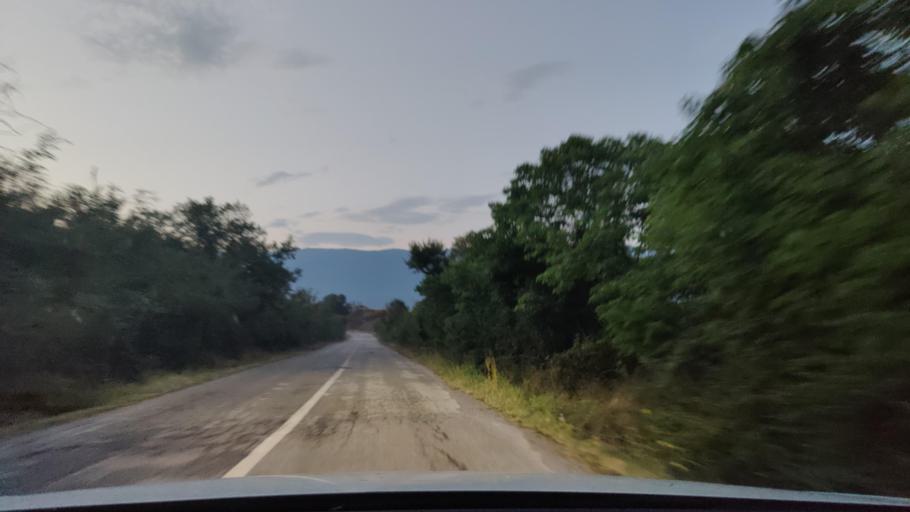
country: GR
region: Central Macedonia
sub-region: Nomos Serron
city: Chrysochorafa
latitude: 41.2013
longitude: 23.0775
